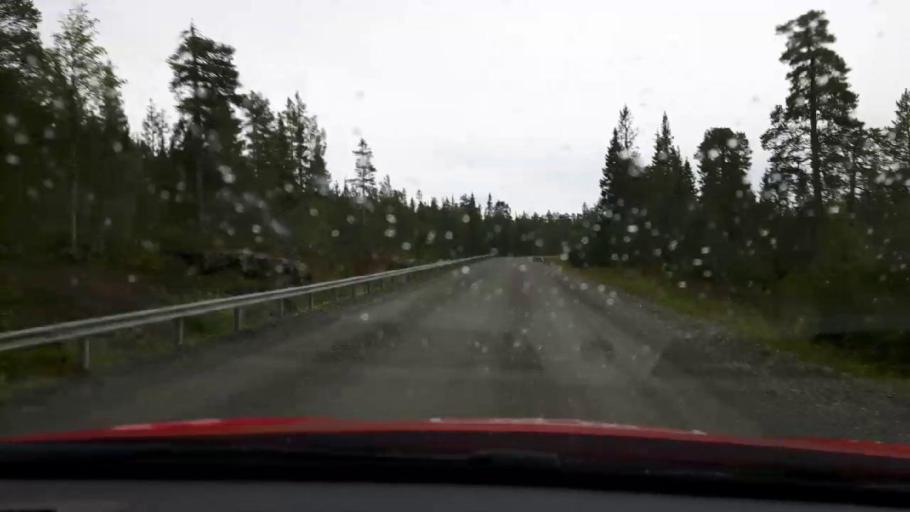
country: NO
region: Nord-Trondelag
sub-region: Meraker
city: Meraker
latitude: 63.6426
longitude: 12.2711
